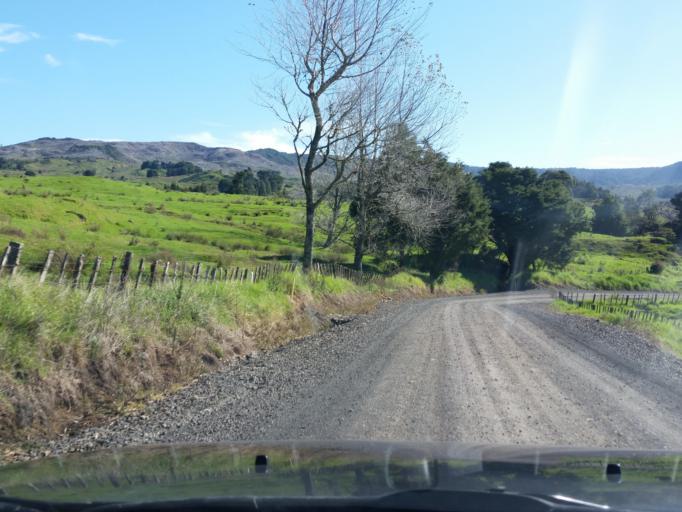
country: NZ
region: Northland
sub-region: Far North District
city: Waimate North
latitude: -35.6044
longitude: 173.7156
